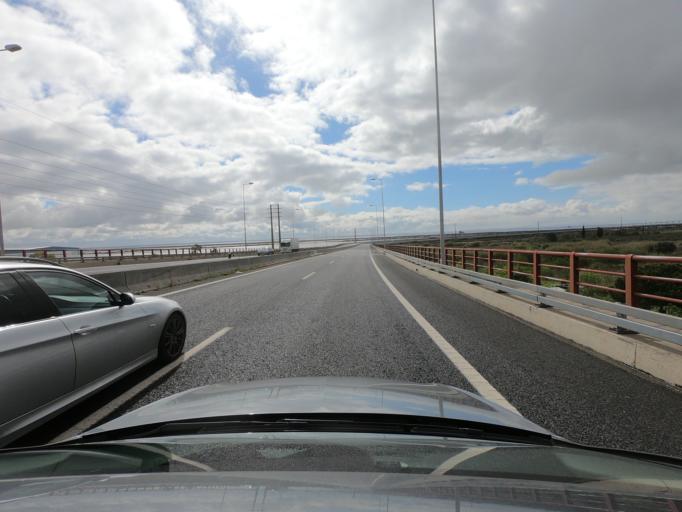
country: PT
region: Lisbon
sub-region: Loures
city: Santa Iria da Azoia
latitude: 38.8451
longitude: -9.0773
